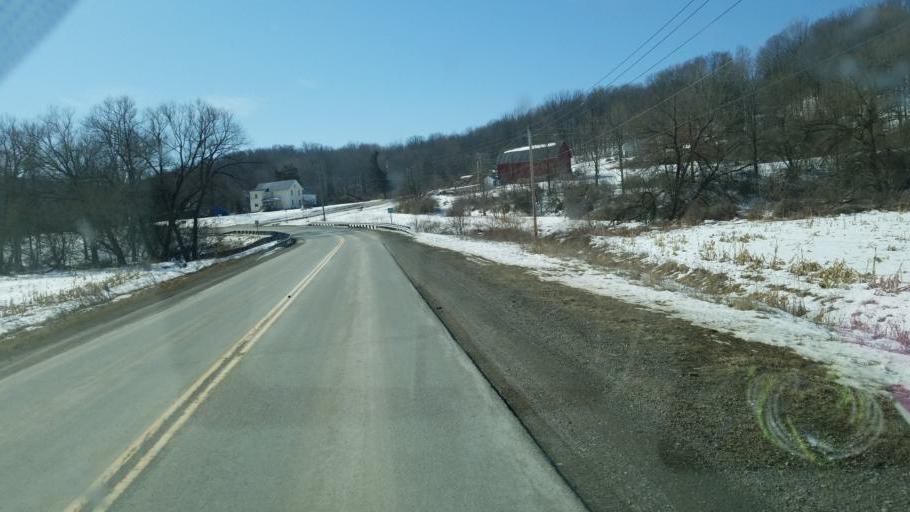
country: US
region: New York
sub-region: Steuben County
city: Hornell
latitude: 42.3738
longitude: -77.6889
